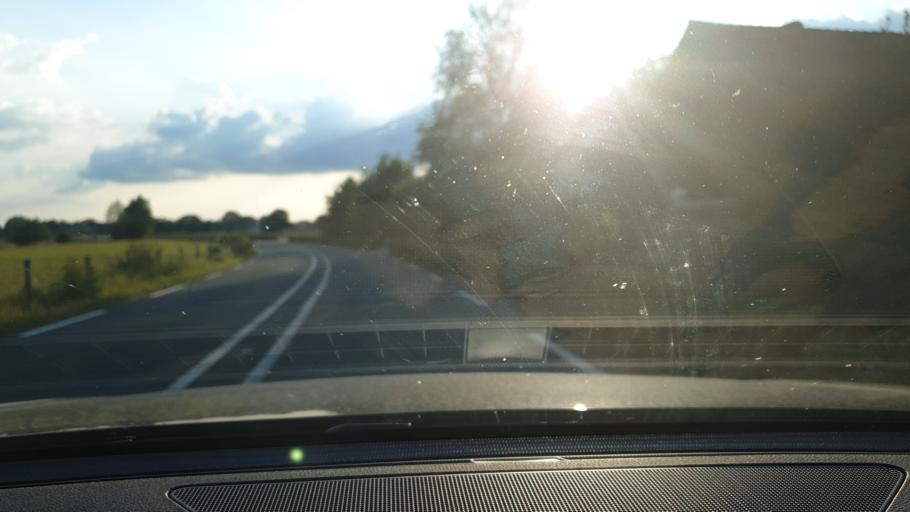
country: NL
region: Limburg
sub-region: Gemeente Gennep
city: Gennep
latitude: 51.7140
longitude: 6.0334
